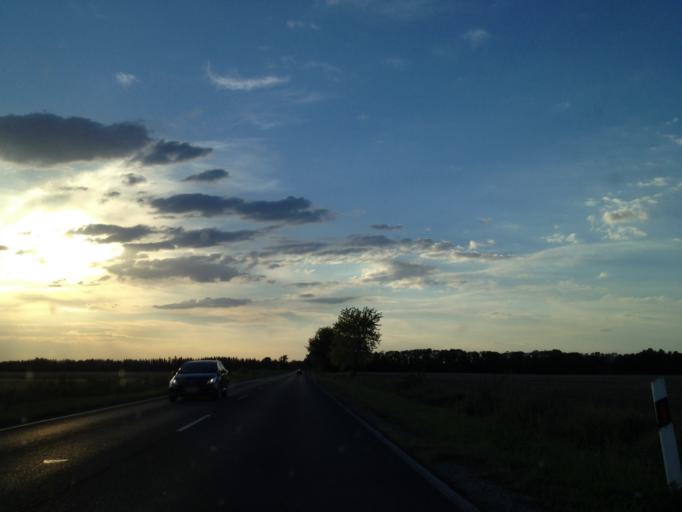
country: HU
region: Gyor-Moson-Sopron
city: Otteveny
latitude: 47.7133
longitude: 17.5148
